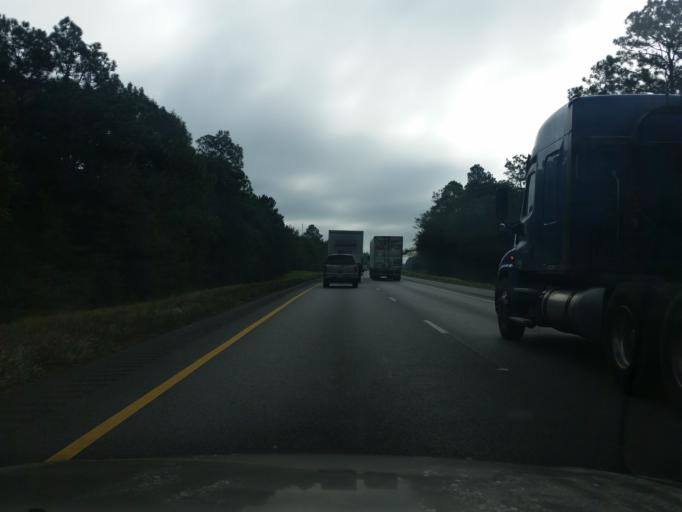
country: US
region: Alabama
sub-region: Baldwin County
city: Loxley
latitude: 30.6506
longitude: -87.7271
